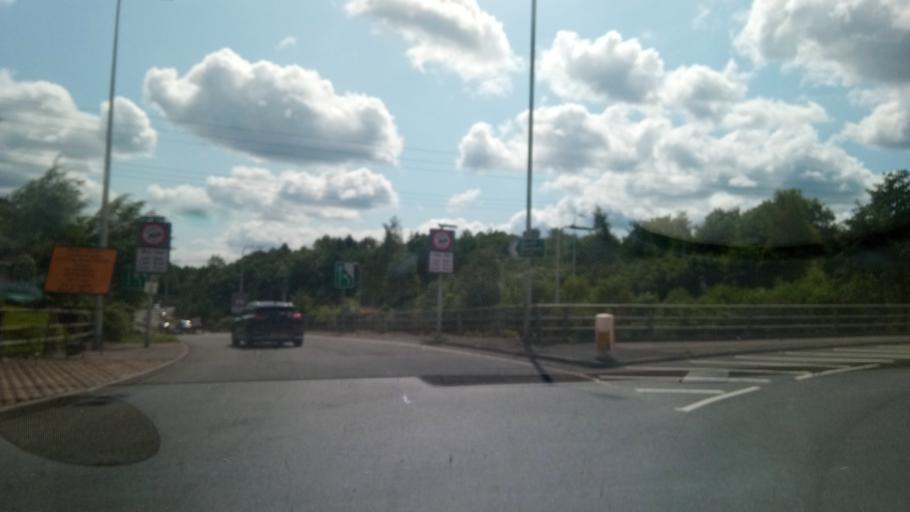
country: GB
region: Wales
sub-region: Rhondda Cynon Taf
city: Pontypridd
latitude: 51.6007
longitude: -3.3306
